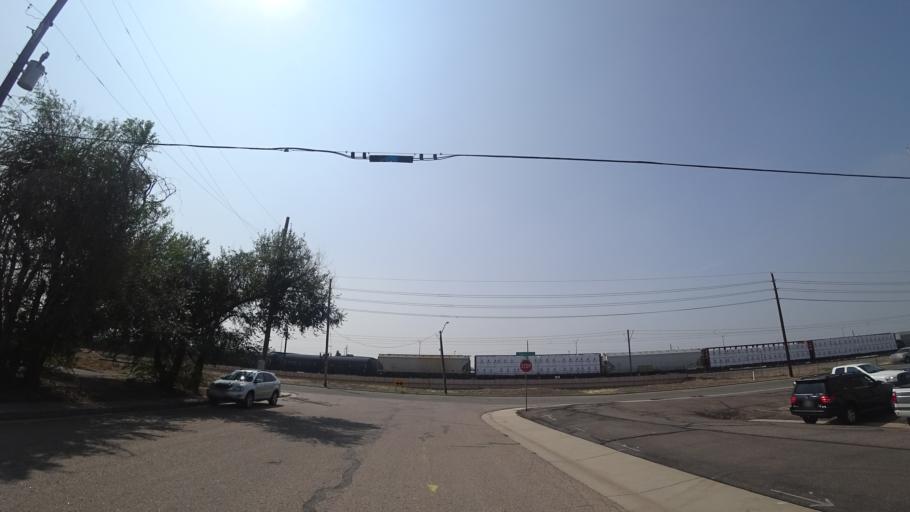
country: US
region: Colorado
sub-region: Arapahoe County
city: Sheridan
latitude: 39.6351
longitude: -105.0066
